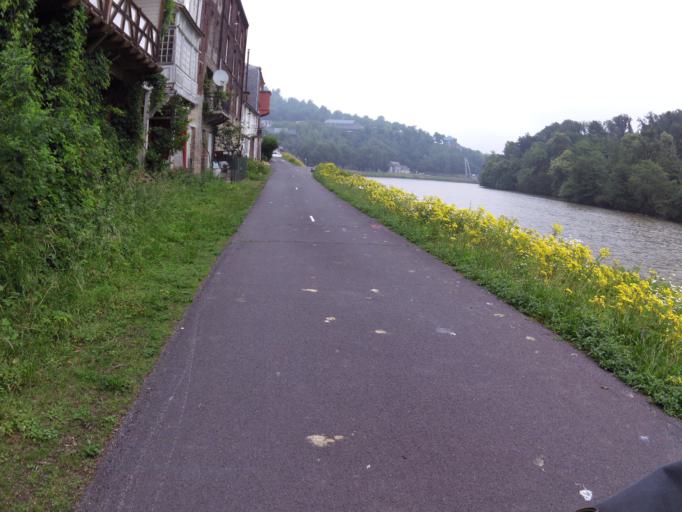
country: FR
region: Champagne-Ardenne
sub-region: Departement des Ardennes
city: Fumay
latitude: 49.9863
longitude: 4.6941
